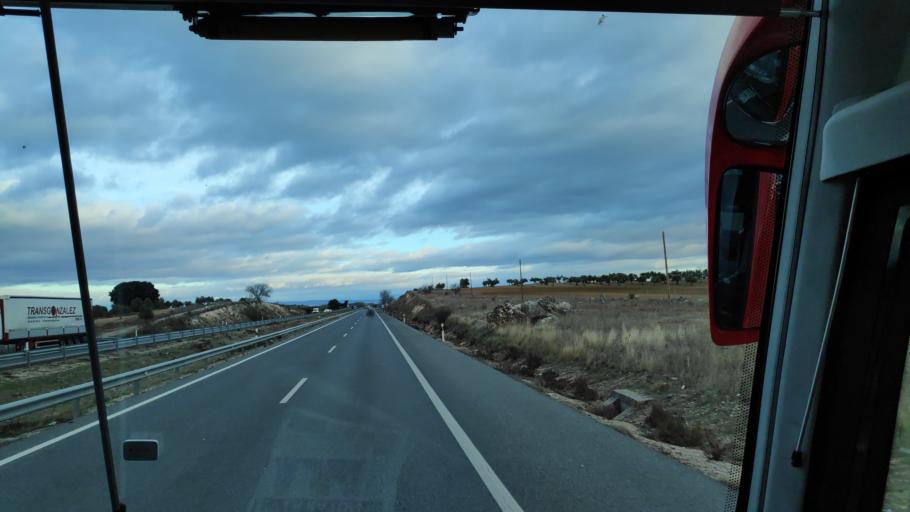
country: ES
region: Madrid
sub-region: Provincia de Madrid
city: Villarejo de Salvanes
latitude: 40.1518
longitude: -3.2422
